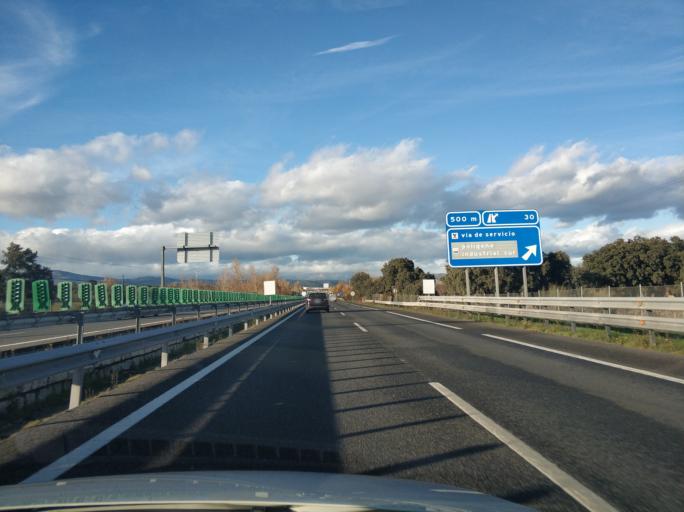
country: ES
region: Madrid
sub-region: Provincia de Madrid
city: San Agustin de Guadalix
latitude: 40.6359
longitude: -3.5912
